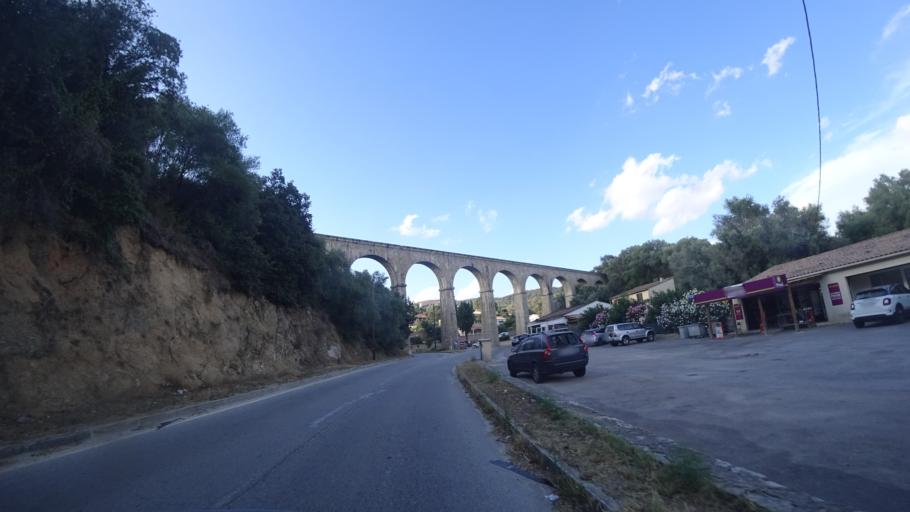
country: FR
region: Corsica
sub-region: Departement de la Corse-du-Sud
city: Ajaccio
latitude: 41.9436
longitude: 8.7351
